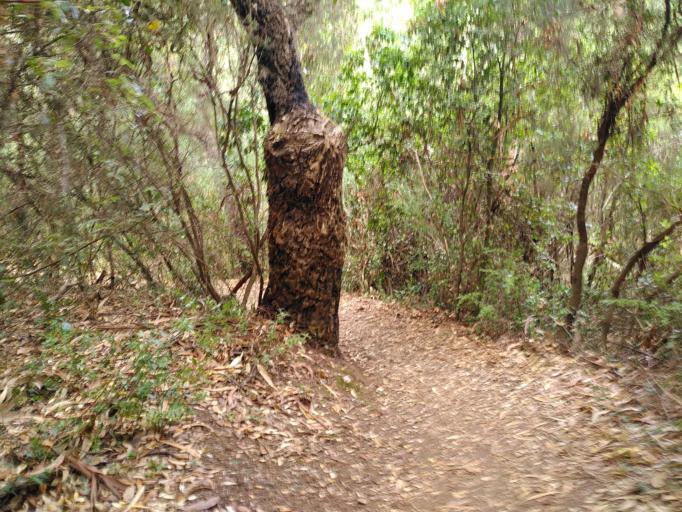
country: FR
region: Provence-Alpes-Cote d'Azur
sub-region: Departement du Var
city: Cavalaire-sur-Mer
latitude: 43.1658
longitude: 6.5113
